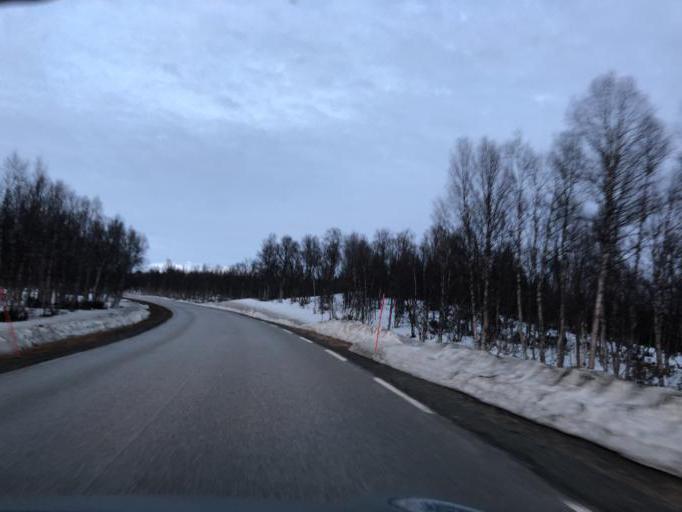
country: NO
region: Sor-Trondelag
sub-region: Tydal
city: Aas
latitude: 62.6996
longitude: 11.7968
